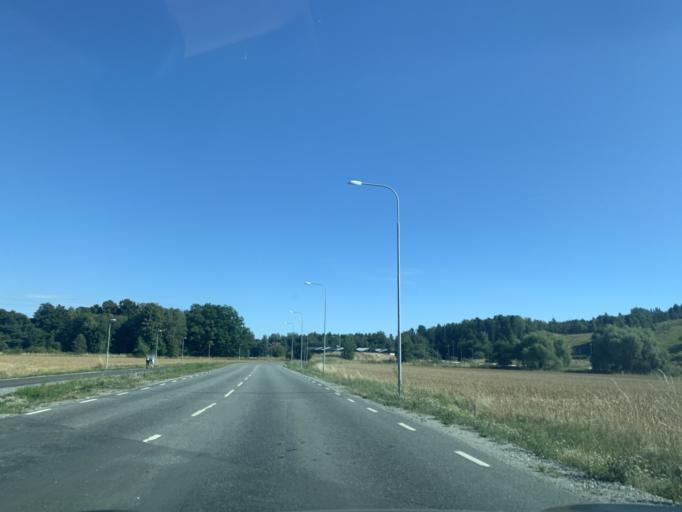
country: SE
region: Stockholm
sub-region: Ekero Kommun
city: Ekeroe
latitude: 59.2831
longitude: 17.8316
